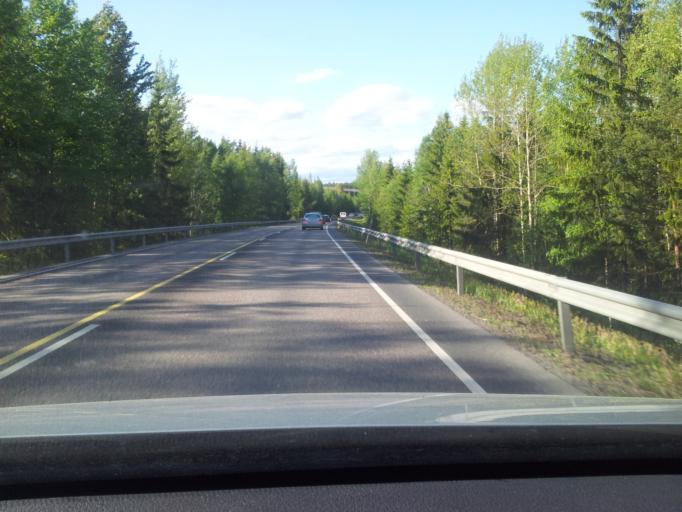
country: FI
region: Kymenlaakso
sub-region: Kouvola
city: Elimaeki
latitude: 60.8468
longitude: 26.5429
